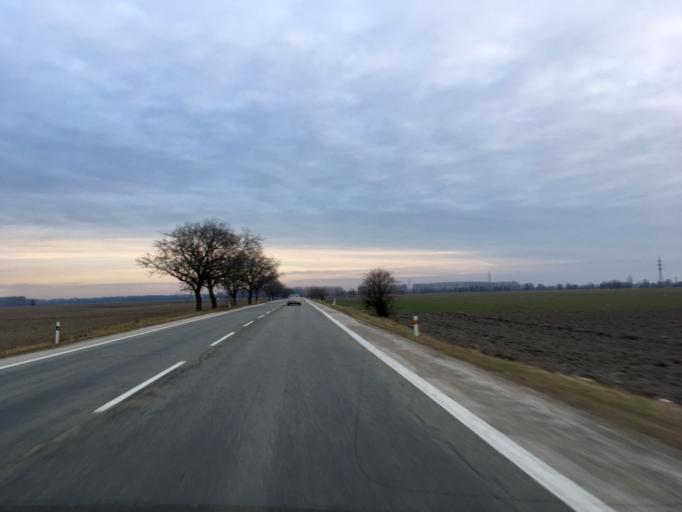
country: SK
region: Trnavsky
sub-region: Okres Dunajska Streda
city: Velky Meder
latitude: 47.9228
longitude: 17.7245
